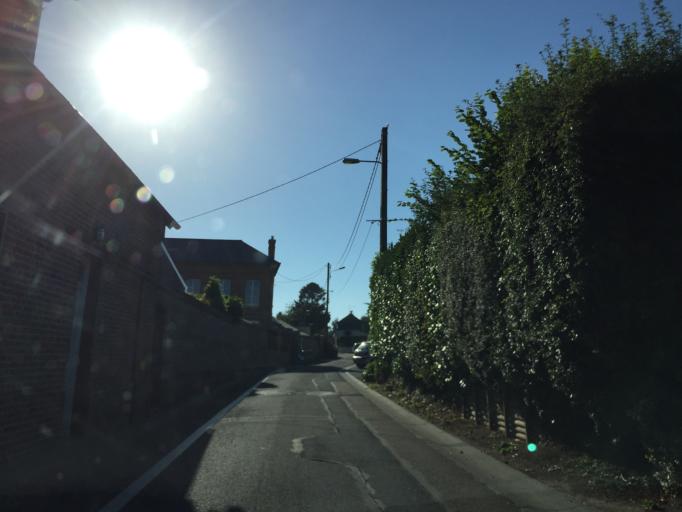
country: FR
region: Lower Normandy
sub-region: Departement du Calvados
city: Equemauville
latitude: 49.3930
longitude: 0.2078
